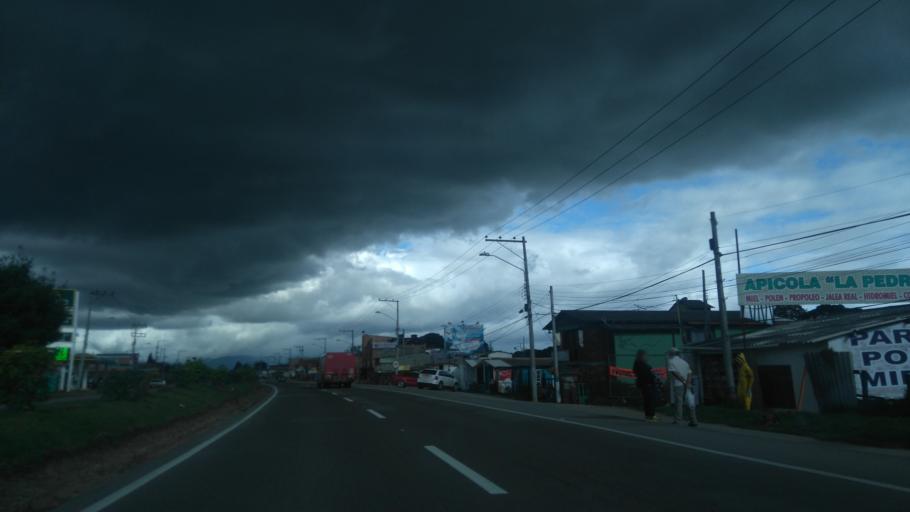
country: CO
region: Cundinamarca
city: El Rosal
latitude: 4.7979
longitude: -74.2081
